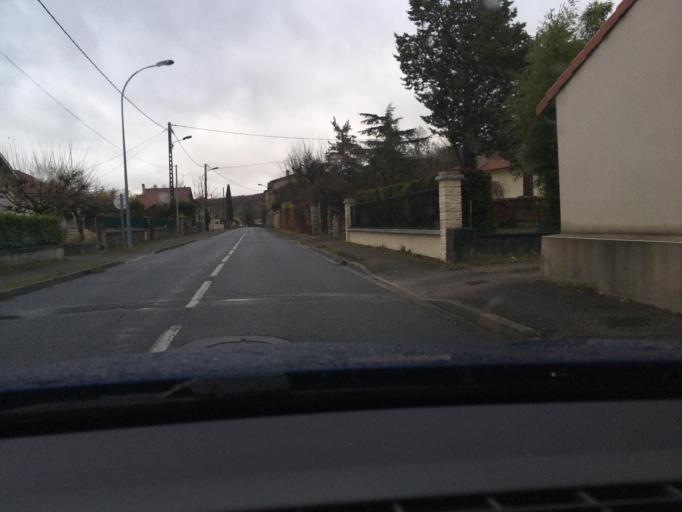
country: FR
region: Midi-Pyrenees
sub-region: Departement de l'Aveyron
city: Villefranche-de-Rouergue
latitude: 44.3616
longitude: 2.0223
